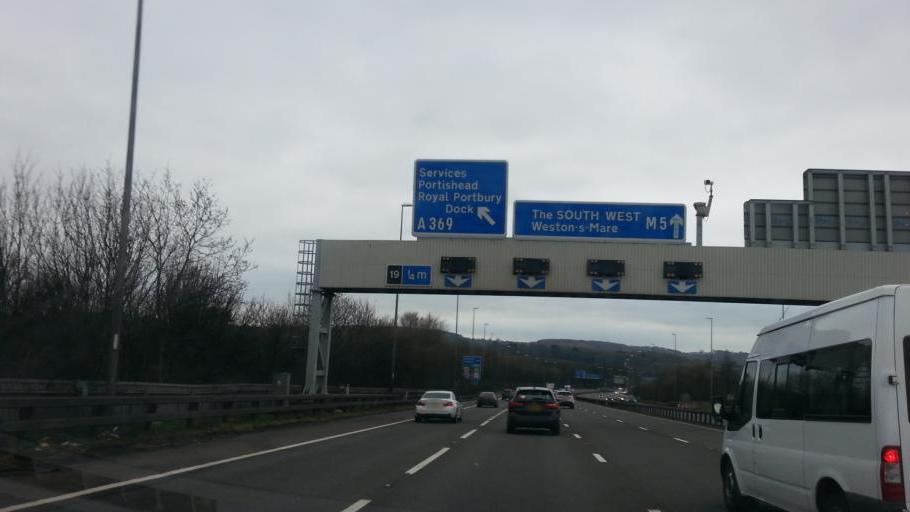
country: GB
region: England
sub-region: North Somerset
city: Easton-in-Gordano
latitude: 51.4836
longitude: -2.6987
